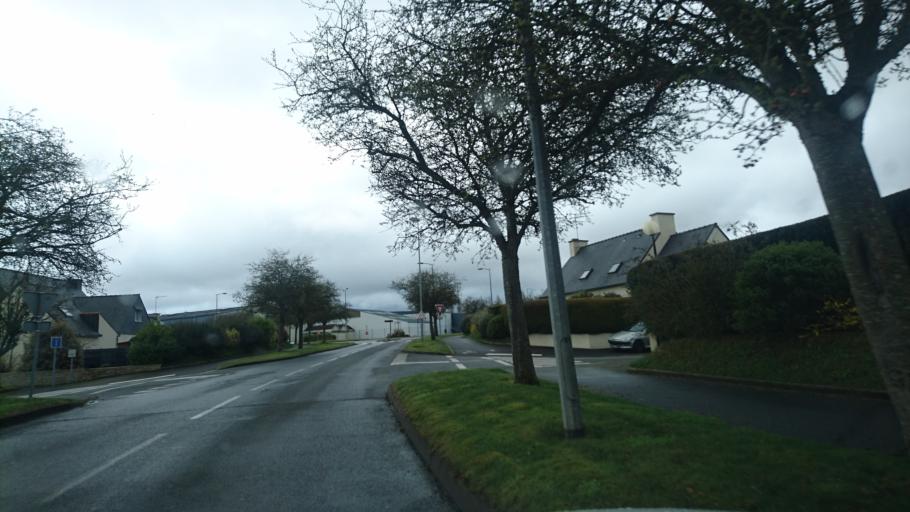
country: FR
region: Brittany
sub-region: Departement des Cotes-d'Armor
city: Lannion
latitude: 48.7327
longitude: -3.4443
